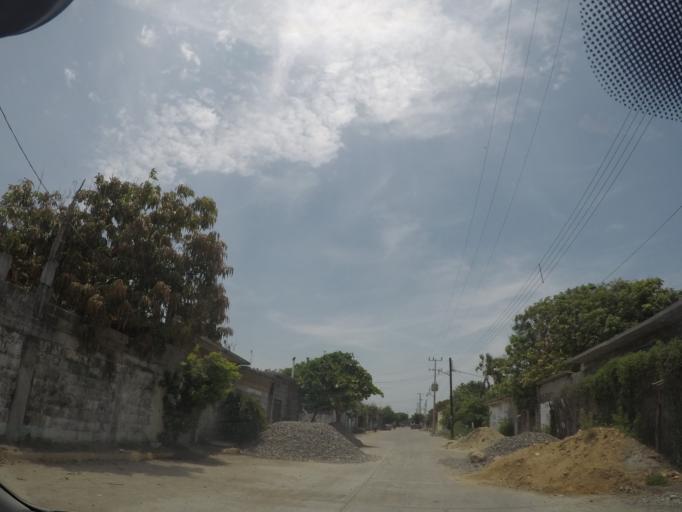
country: MX
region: Oaxaca
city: San Mateo del Mar
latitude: 16.2111
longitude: -94.9833
